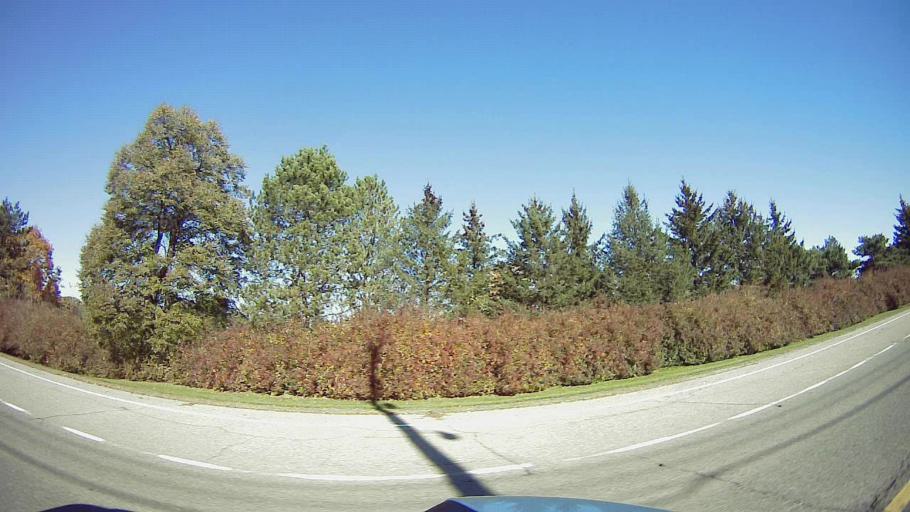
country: US
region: Michigan
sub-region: Oakland County
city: Franklin
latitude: 42.5438
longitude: -83.3255
